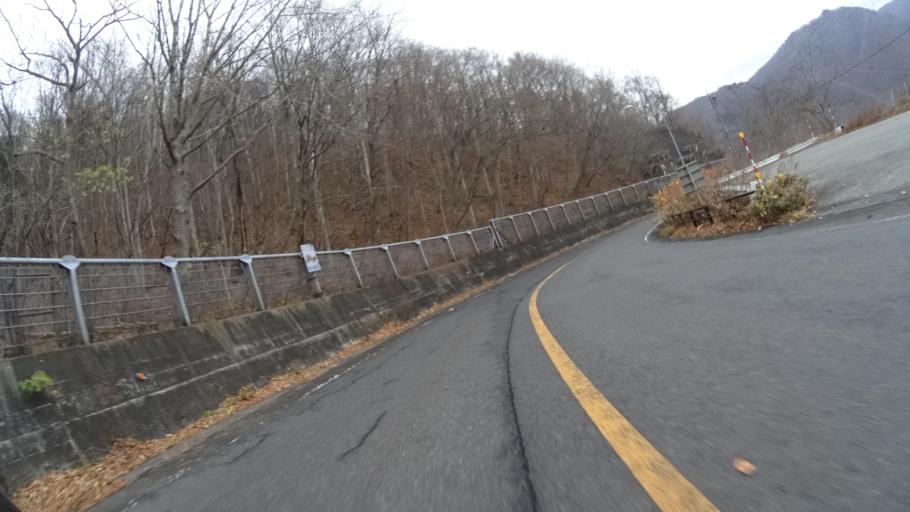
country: JP
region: Gunma
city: Nakanojomachi
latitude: 36.7412
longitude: 138.8350
